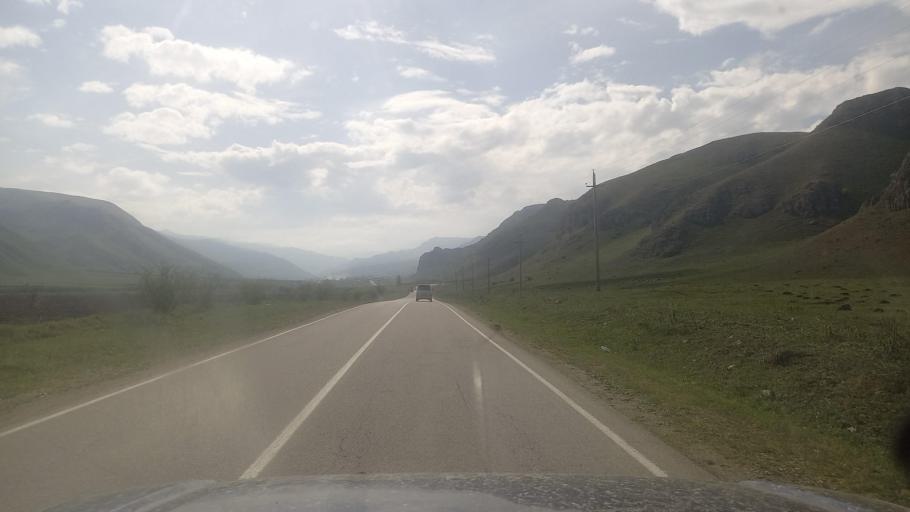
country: RU
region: Kabardino-Balkariya
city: Kamennomostskoye
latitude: 43.7346
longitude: 42.9789
